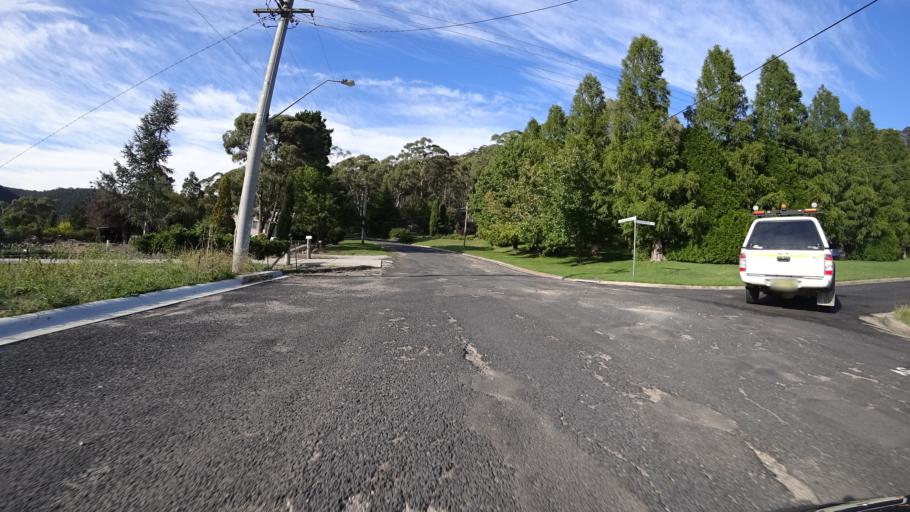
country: AU
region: New South Wales
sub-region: Lithgow
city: Lithgow
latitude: -33.4932
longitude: 150.1500
